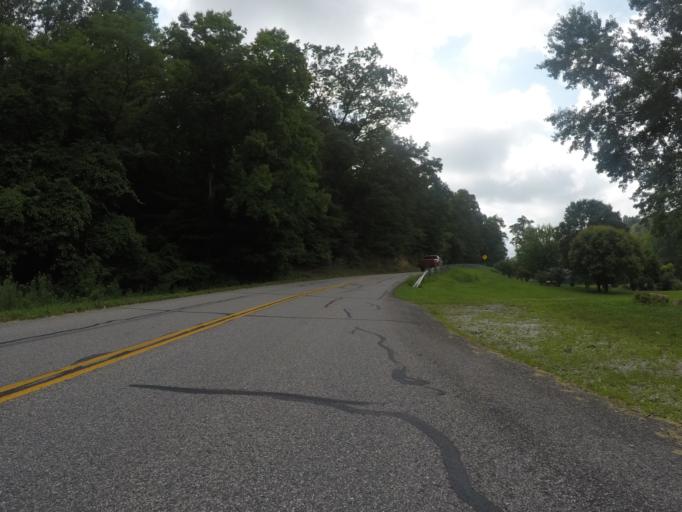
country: US
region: Kentucky
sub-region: Boyd County
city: Meads
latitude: 38.4107
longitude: -82.6696
